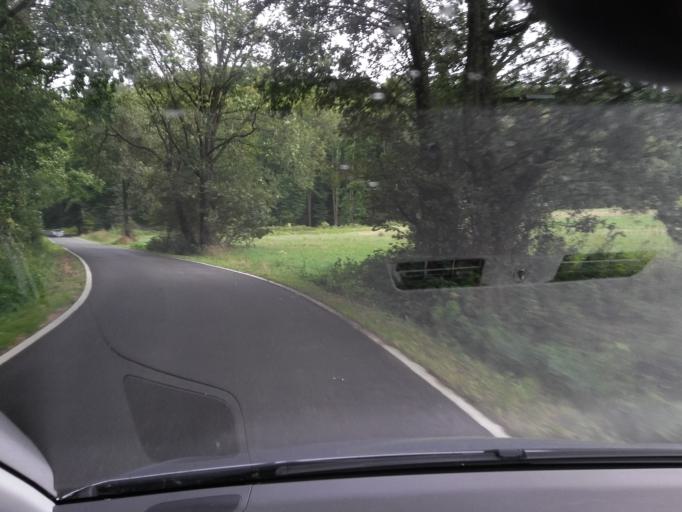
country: BE
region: Wallonia
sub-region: Province du Luxembourg
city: Arlon
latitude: 49.7200
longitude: 5.8176
